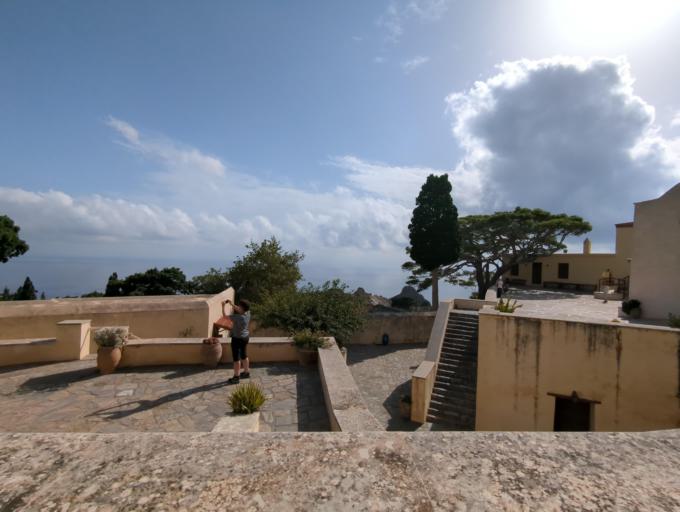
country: GR
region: Crete
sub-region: Nomos Rethymnis
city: Atsipopoulon
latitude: 35.1576
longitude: 24.4566
